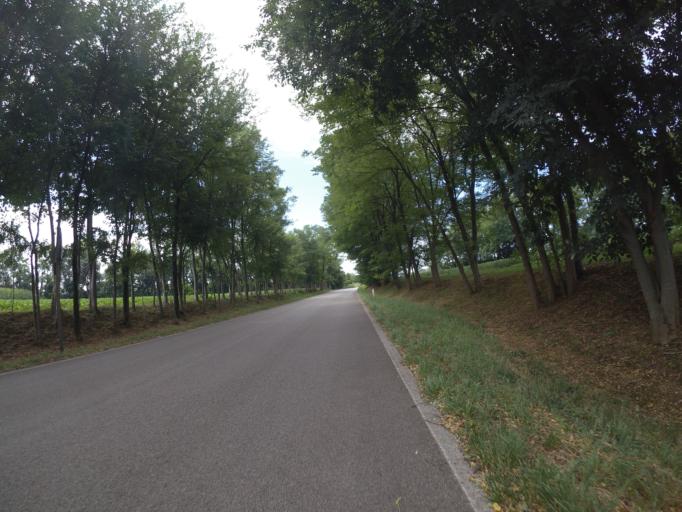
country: IT
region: Friuli Venezia Giulia
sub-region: Provincia di Udine
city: Bertiolo
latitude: 45.9718
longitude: 13.0885
